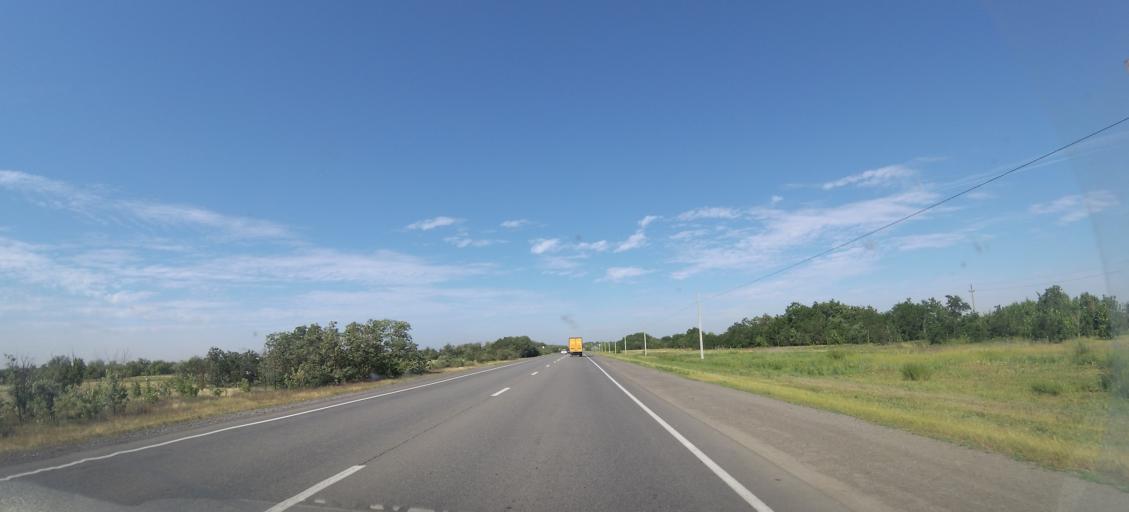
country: RU
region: Volgograd
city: Oktyabr'skiy
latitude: 48.6913
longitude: 43.7776
